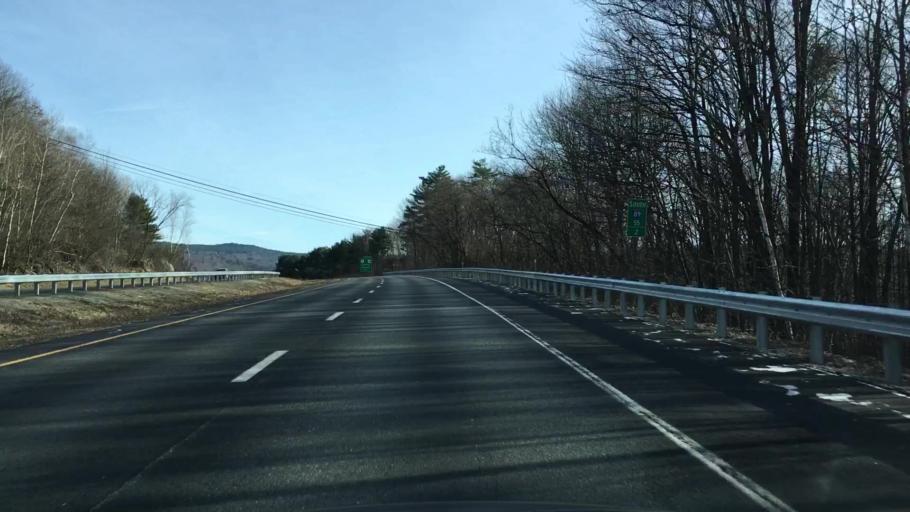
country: US
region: New Hampshire
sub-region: Grafton County
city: Lebanon
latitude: 43.6426
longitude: -72.2293
